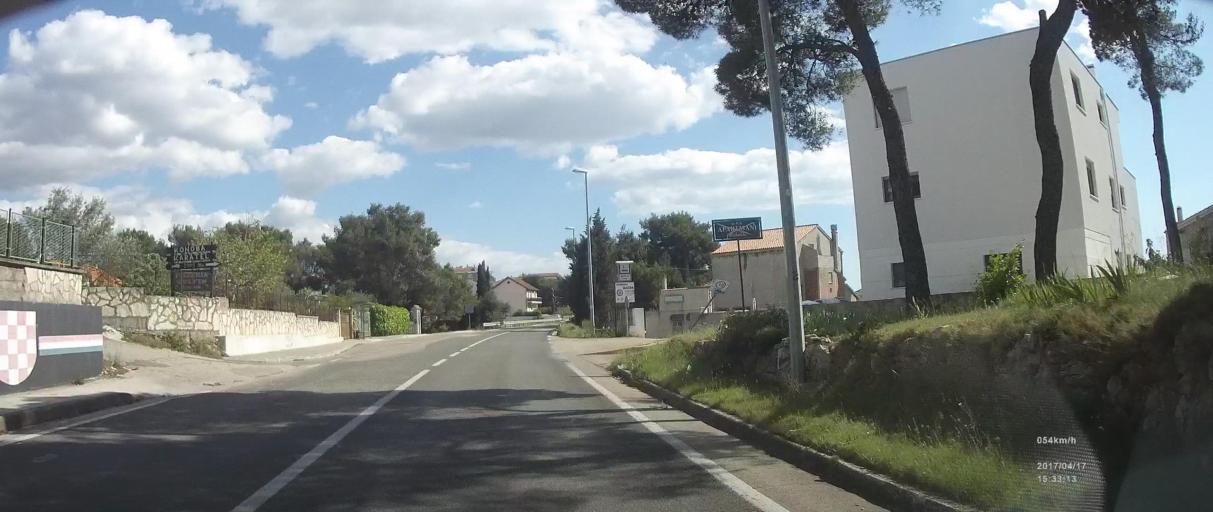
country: HR
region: Sibensko-Kniniska
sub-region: Grad Sibenik
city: Brodarica
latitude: 43.6879
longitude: 15.9108
